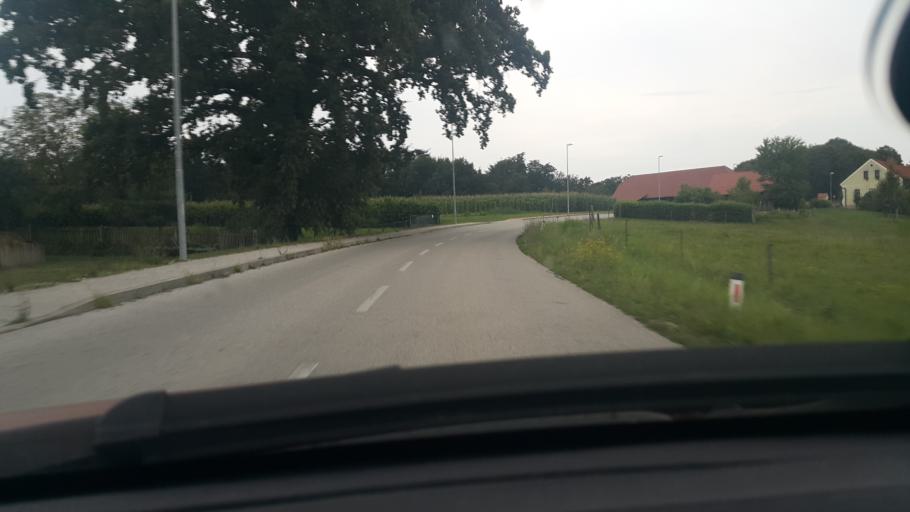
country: SI
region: Brezice
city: Brezice
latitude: 45.9239
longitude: 15.6683
